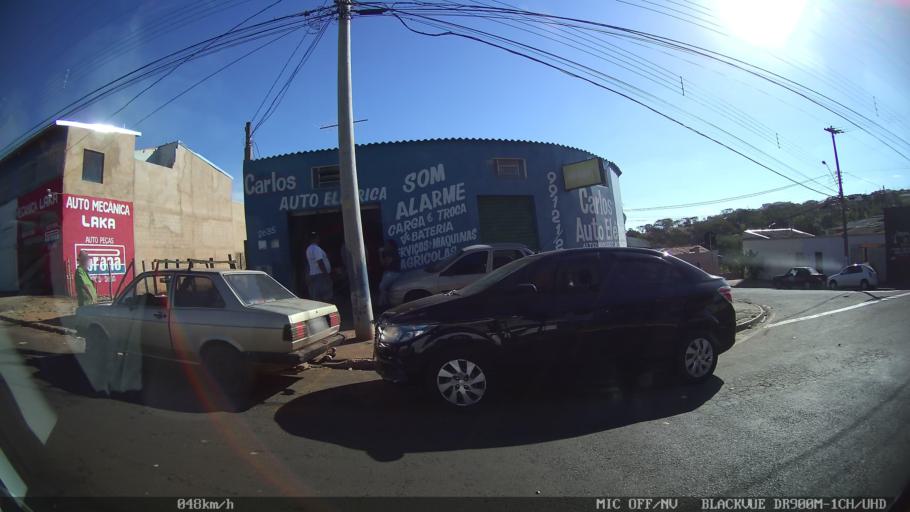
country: BR
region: Sao Paulo
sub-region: Franca
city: Franca
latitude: -20.4903
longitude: -47.4286
